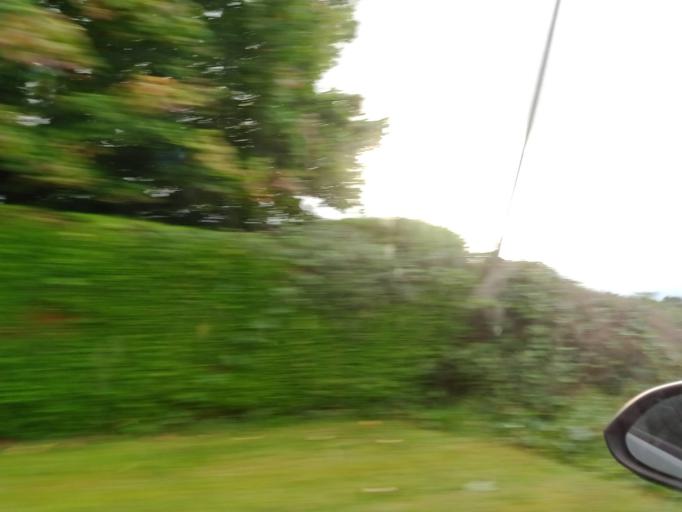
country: IE
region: Leinster
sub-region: Laois
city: Mountmellick
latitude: 53.1285
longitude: -7.3871
